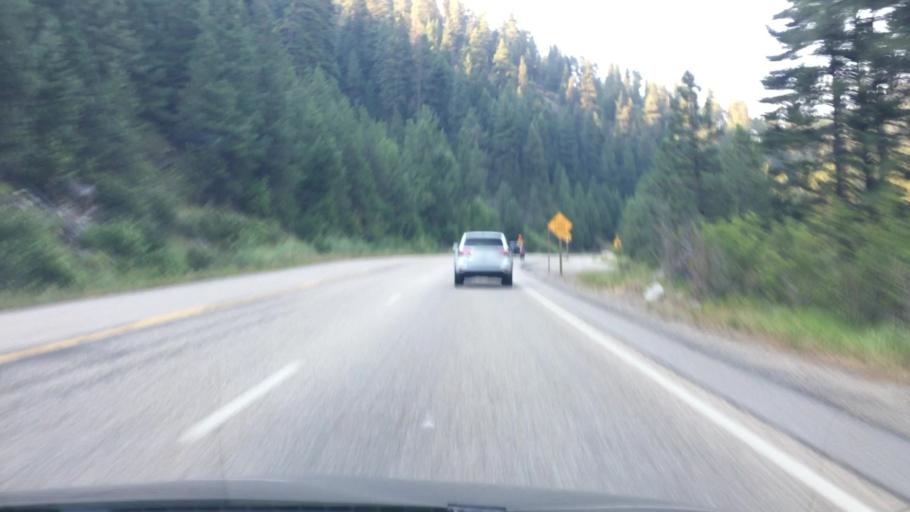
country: US
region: Idaho
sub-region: Valley County
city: Cascade
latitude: 44.1740
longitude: -116.1200
